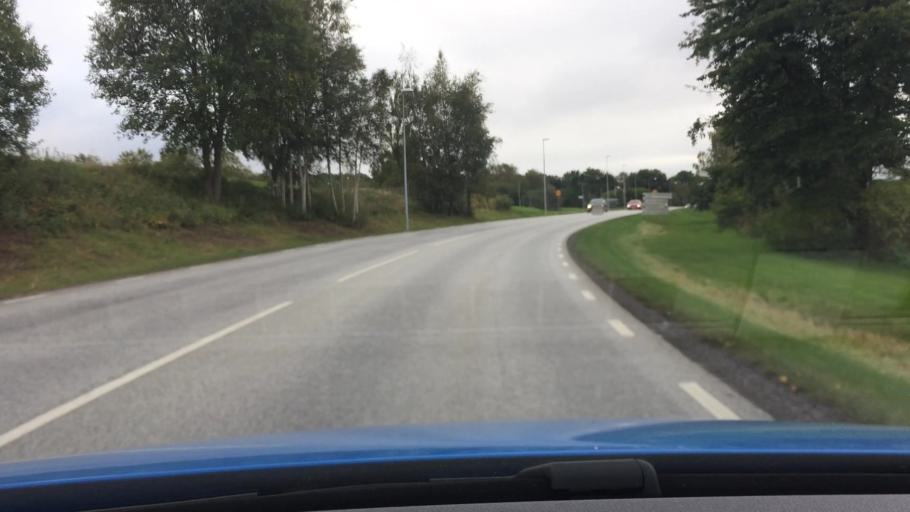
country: SE
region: Halland
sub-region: Kungsbacka Kommun
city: Kungsbacka
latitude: 57.4911
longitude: 12.0914
